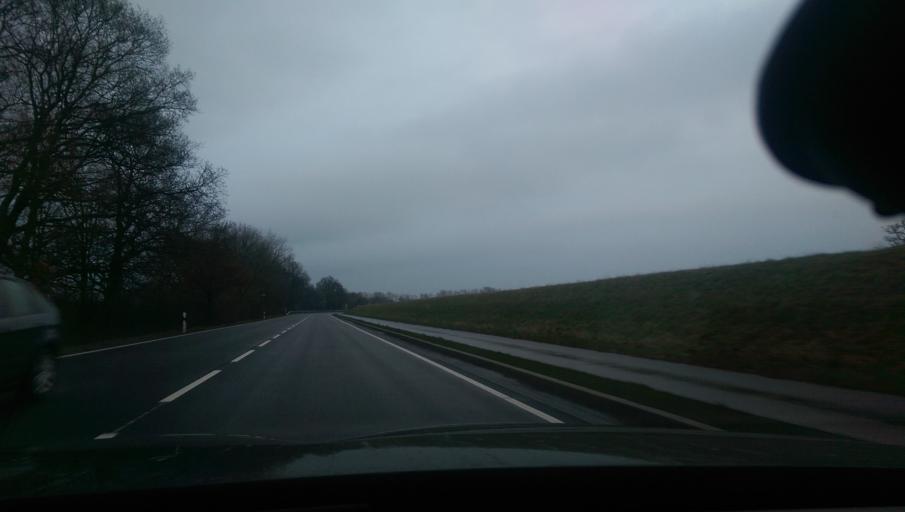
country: DE
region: Lower Saxony
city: Dorverden
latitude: 52.8759
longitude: 9.2248
